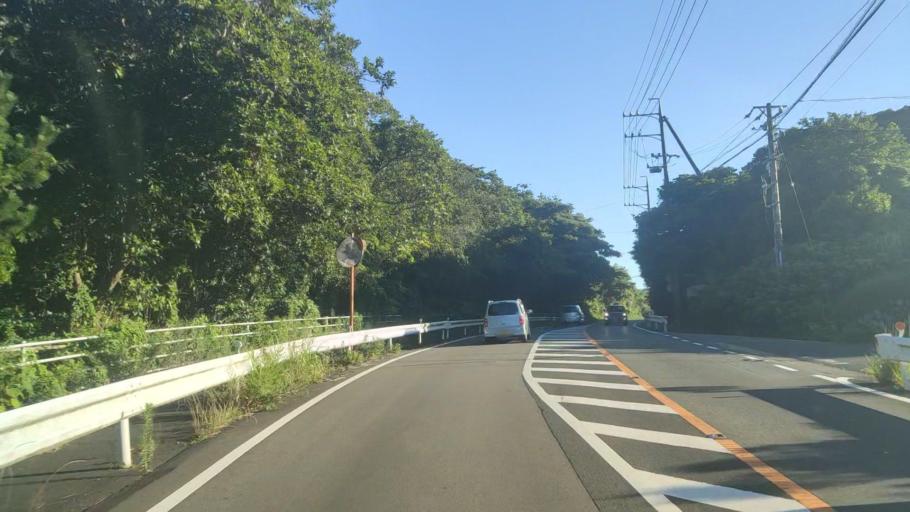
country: JP
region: Mie
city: Toba
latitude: 34.2648
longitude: 136.8674
